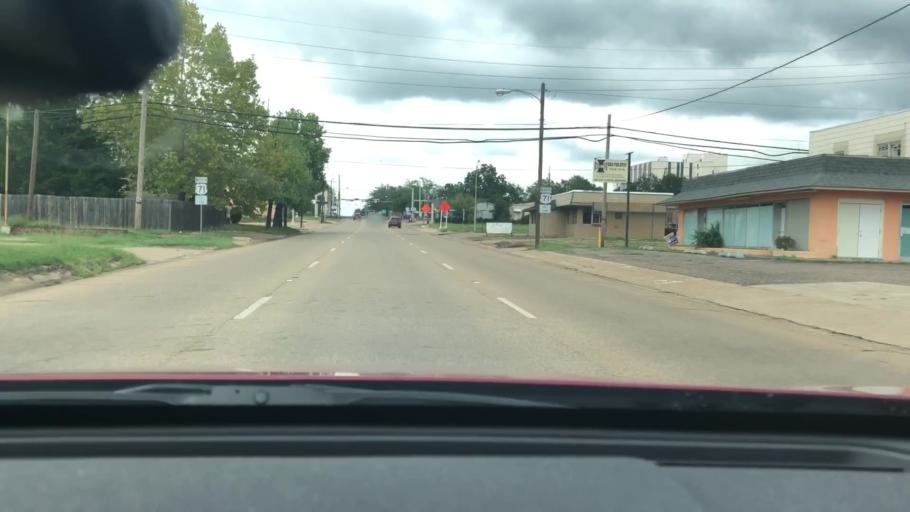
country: US
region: Texas
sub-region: Bowie County
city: Texarkana
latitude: 33.4261
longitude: -94.0456
